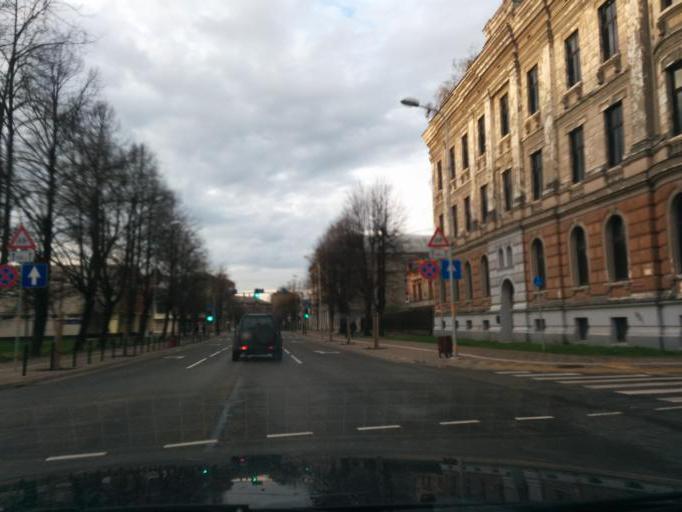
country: LV
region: Jelgava
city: Jelgava
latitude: 56.6437
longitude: 23.7311
